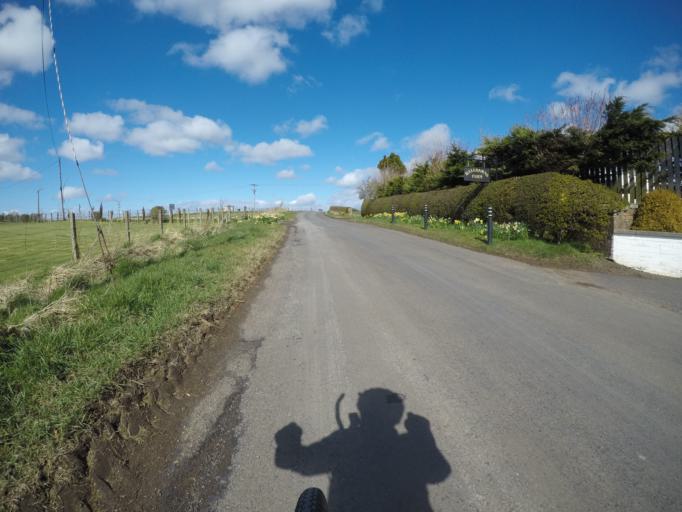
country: GB
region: Scotland
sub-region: East Ayrshire
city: Crosshouse
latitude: 55.6066
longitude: -4.5751
